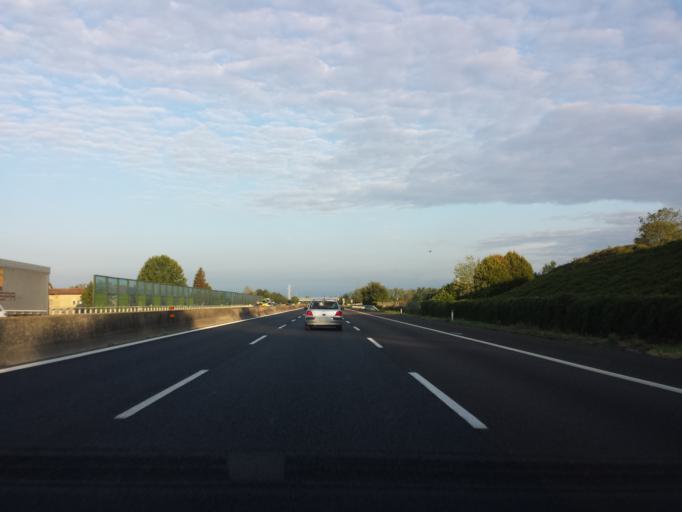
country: IT
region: Lombardy
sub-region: Provincia di Bergamo
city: Costa di Mezzate
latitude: 45.6465
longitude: 9.7944
